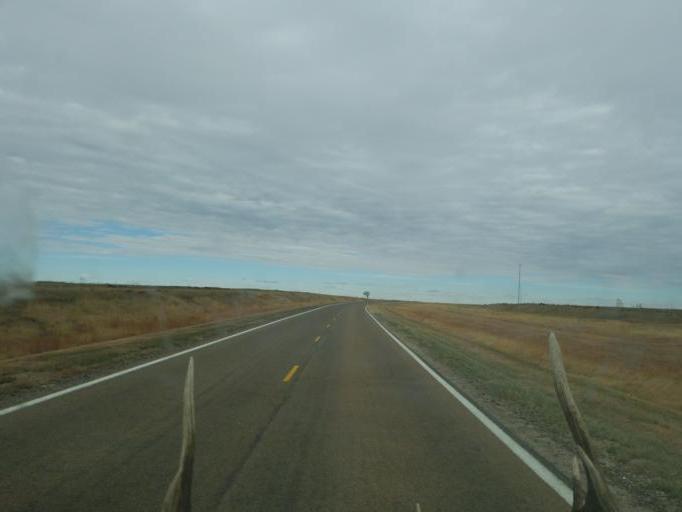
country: US
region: Kansas
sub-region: Thomas County
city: Colby
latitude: 39.0453
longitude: -101.2689
